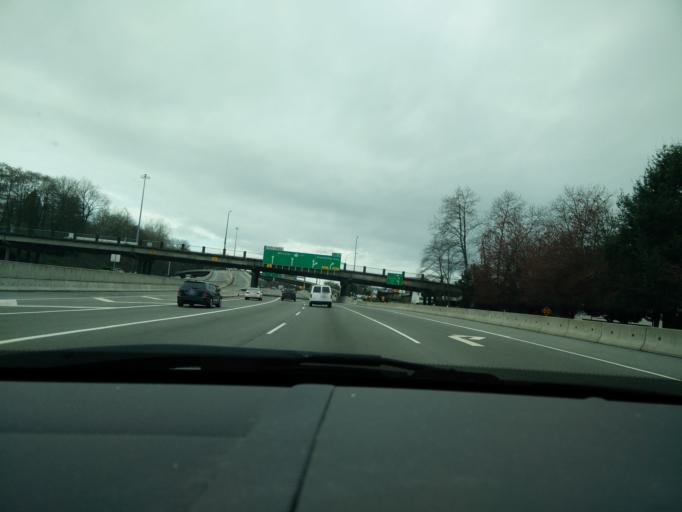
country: CA
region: British Columbia
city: Burnaby
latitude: 49.2579
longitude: -123.0104
